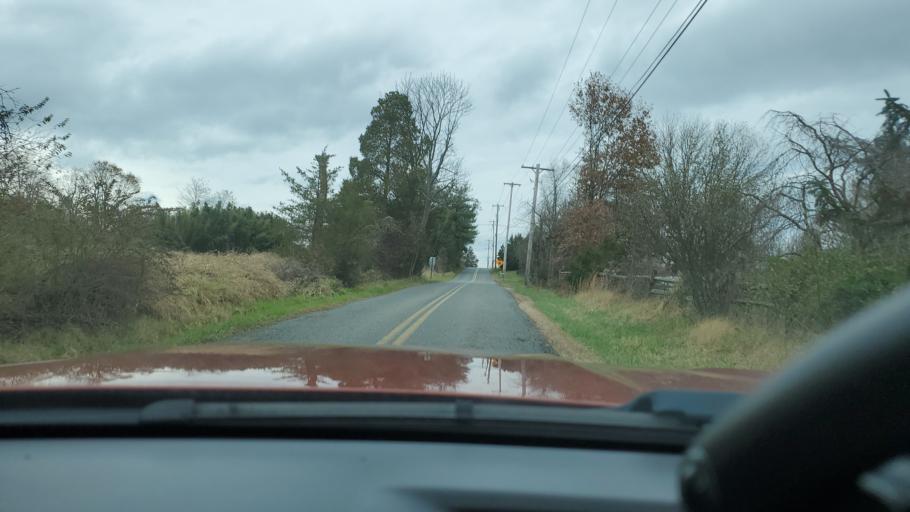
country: US
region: Pennsylvania
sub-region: Montgomery County
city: Spring Mount
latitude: 40.2976
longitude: -75.5014
